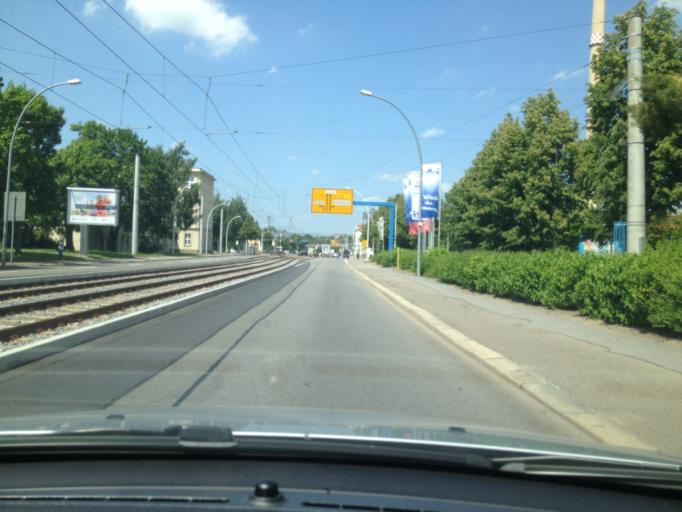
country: DE
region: Saxony
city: Chemnitz
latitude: 50.7952
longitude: 12.9204
